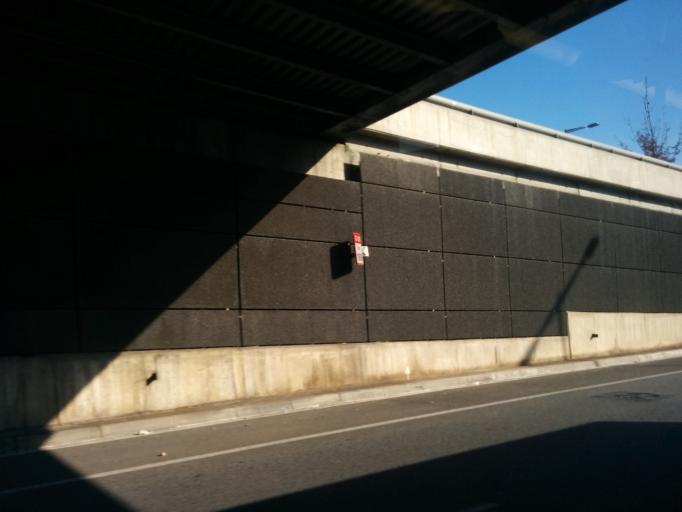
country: ES
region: Catalonia
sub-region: Provincia de Barcelona
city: les Corts
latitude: 41.3610
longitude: 2.1306
